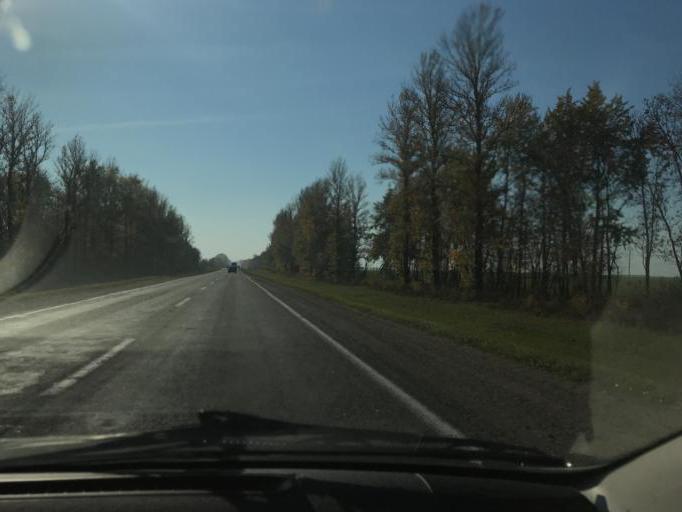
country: BY
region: Minsk
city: Salihorsk
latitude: 52.8968
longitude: 27.4744
